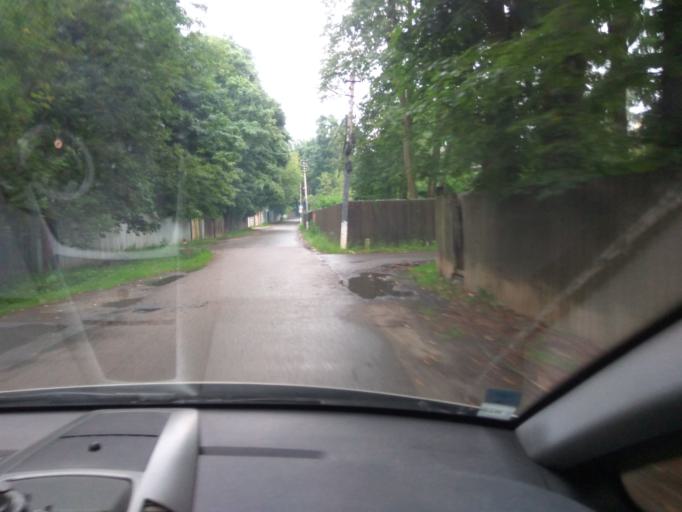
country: RU
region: Moskovskaya
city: Bykovo
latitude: 55.6268
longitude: 38.0814
